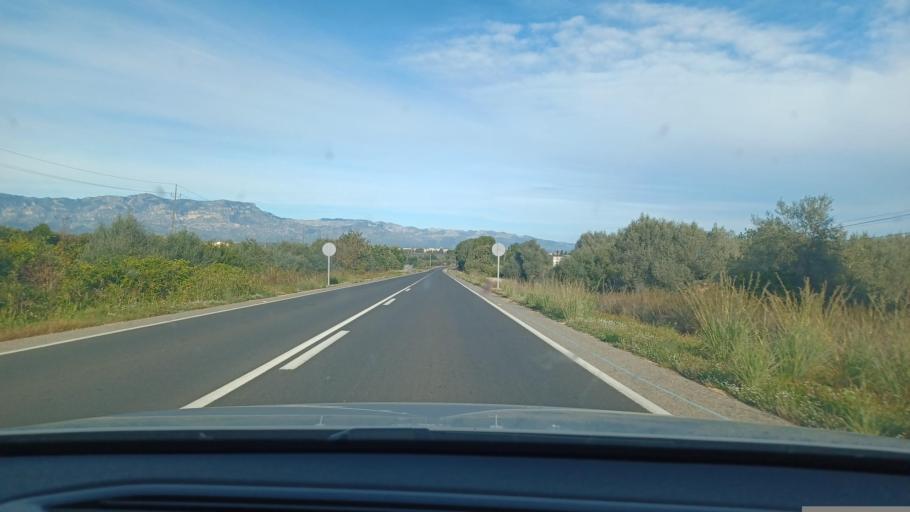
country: ES
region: Catalonia
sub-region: Provincia de Tarragona
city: Santa Barbara
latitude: 40.6839
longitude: 0.5099
